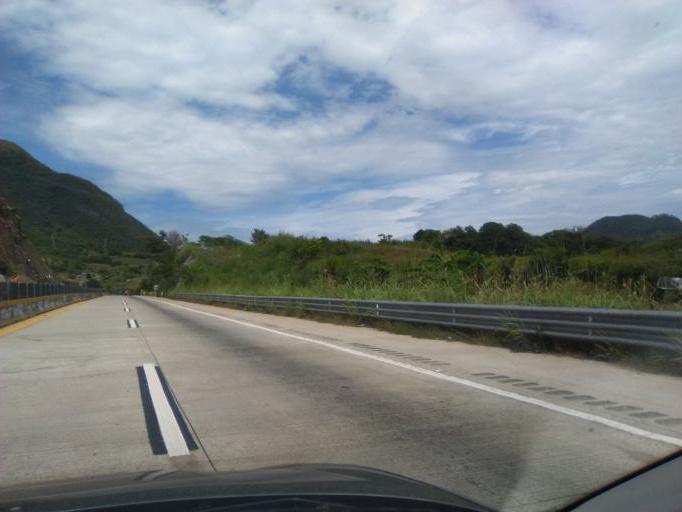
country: MX
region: Guerrero
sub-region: Chilpancingo de los Bravo
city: Julian Blanco (Dos Caminos)
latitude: 17.2173
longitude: -99.5298
